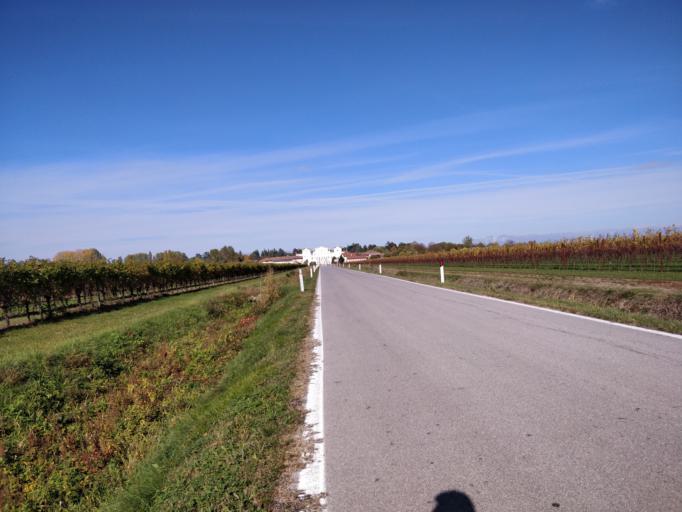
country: IT
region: Friuli Venezia Giulia
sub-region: Provincia di Udine
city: Codroipo
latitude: 45.9420
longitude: 13.0112
